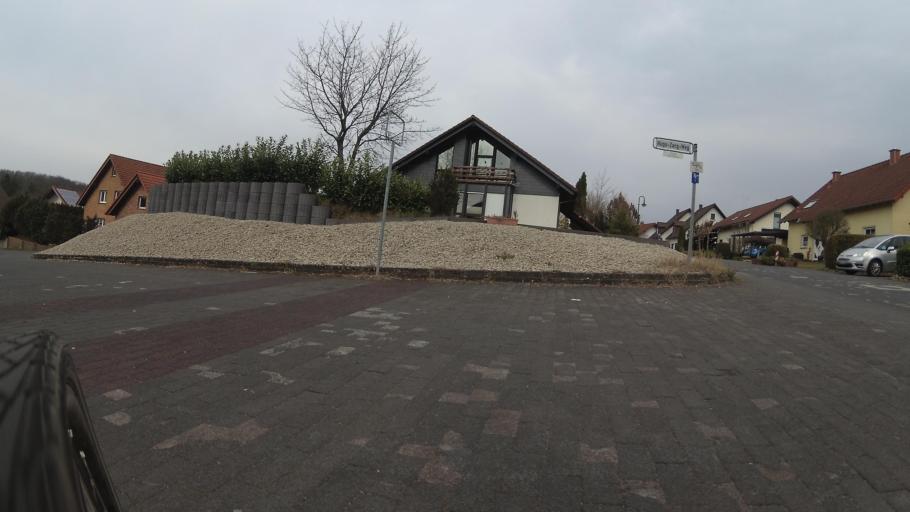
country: DE
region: Rheinland-Pfalz
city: Birkenfeld
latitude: 49.6551
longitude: 7.1720
